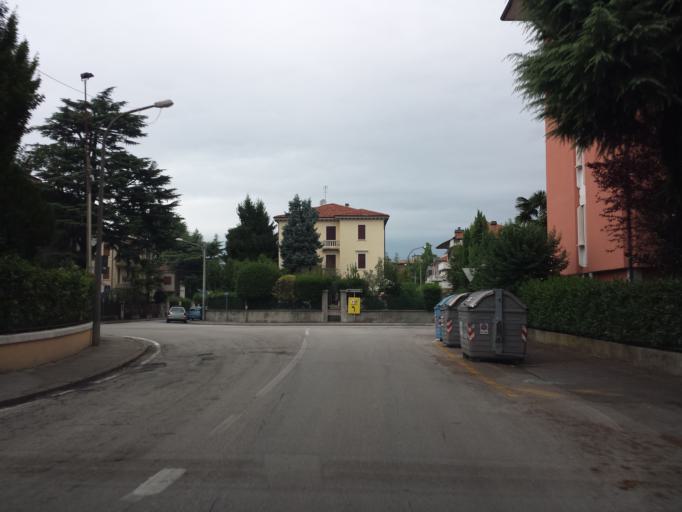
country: IT
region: Veneto
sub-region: Provincia di Vicenza
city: Vicenza
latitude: 45.5505
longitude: 11.5591
